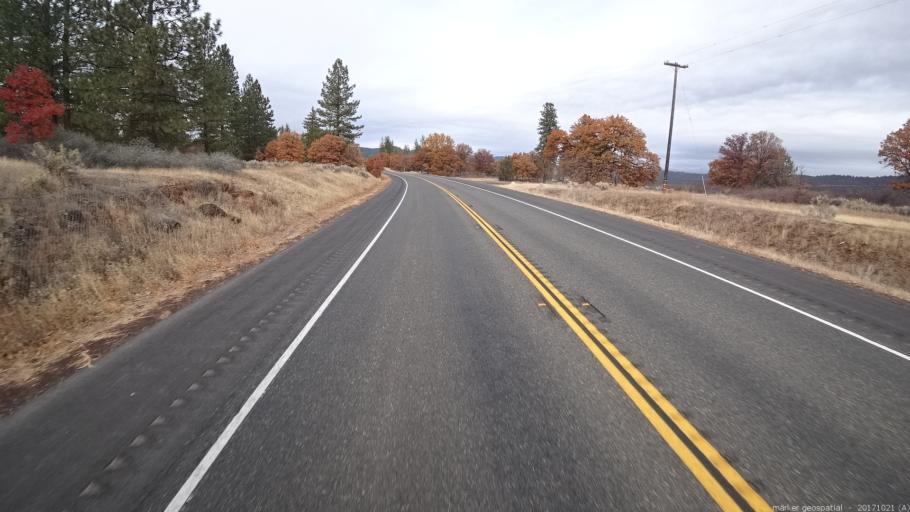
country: US
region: California
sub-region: Shasta County
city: Burney
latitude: 41.0445
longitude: -121.6316
